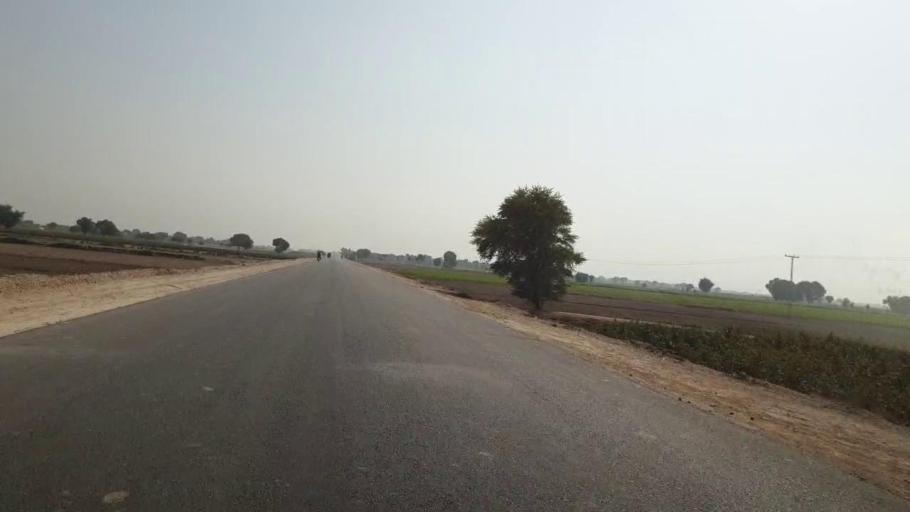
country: PK
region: Sindh
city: Dadu
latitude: 26.6576
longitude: 67.7764
